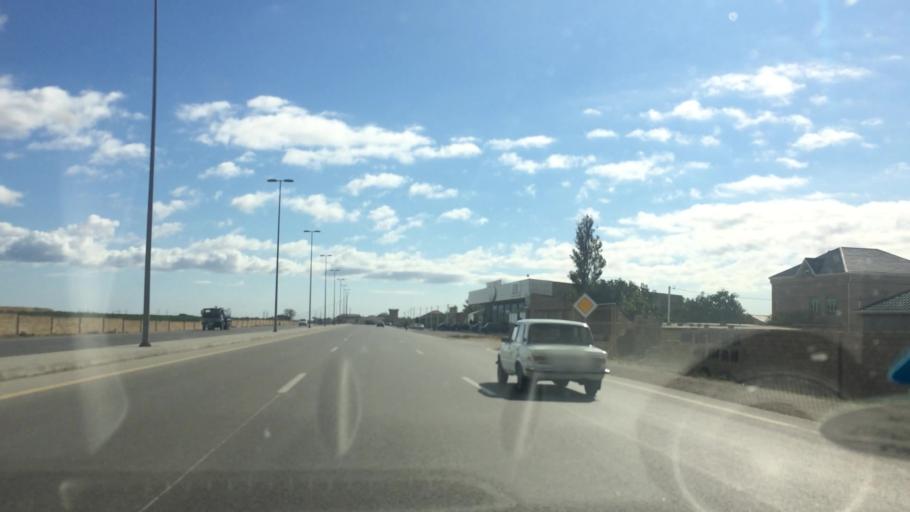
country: AZ
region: Baki
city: Qala
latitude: 40.4497
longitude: 50.1603
